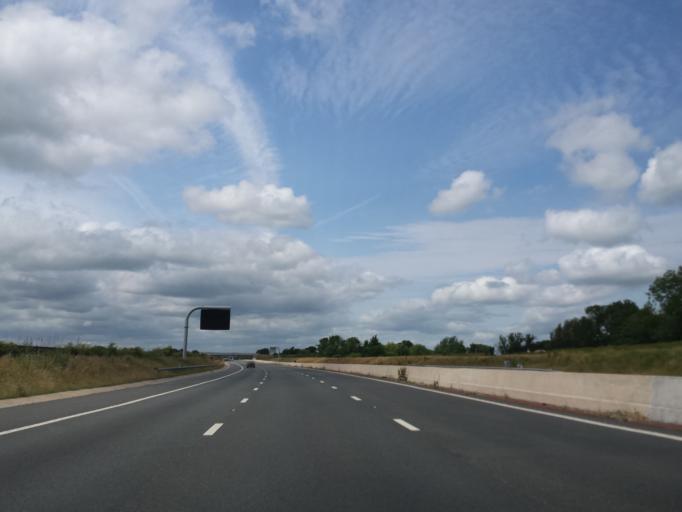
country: GB
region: England
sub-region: North Yorkshire
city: Bedale
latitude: 54.2782
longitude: -1.5325
